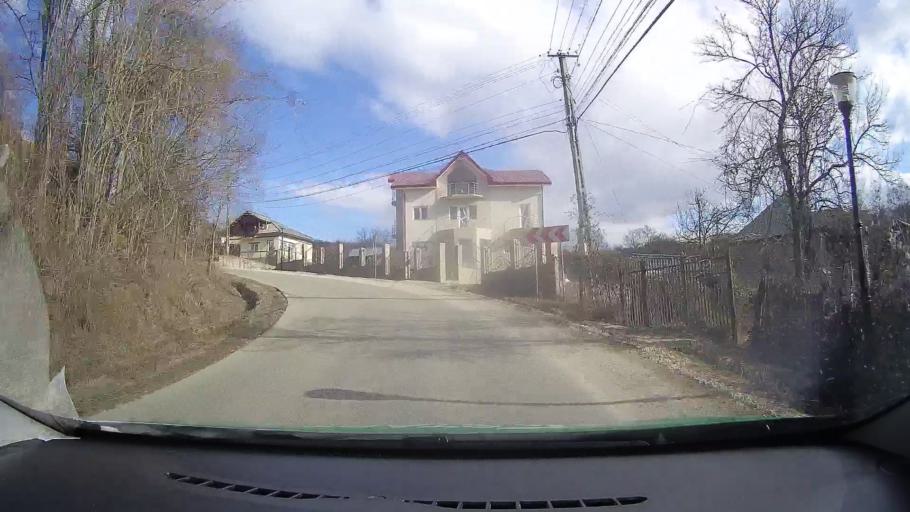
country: RO
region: Dambovita
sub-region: Comuna Varfuri
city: Varfuri
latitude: 45.0929
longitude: 25.5081
